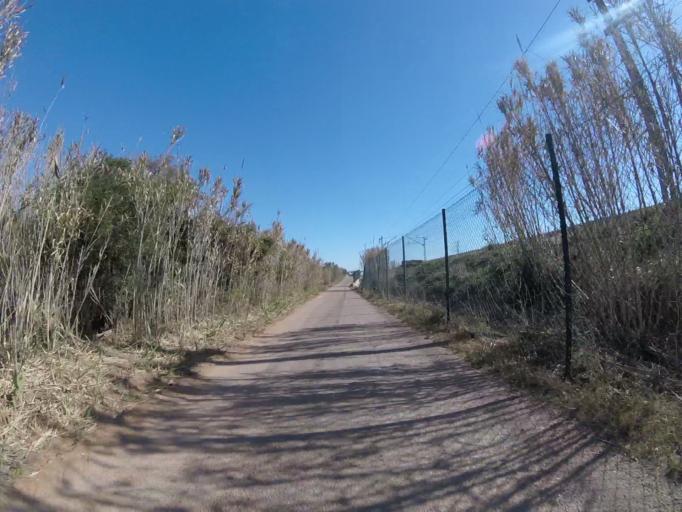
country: ES
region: Valencia
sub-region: Provincia de Castello
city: Santa Magdalena de Pulpis
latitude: 40.3452
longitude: 0.2699
